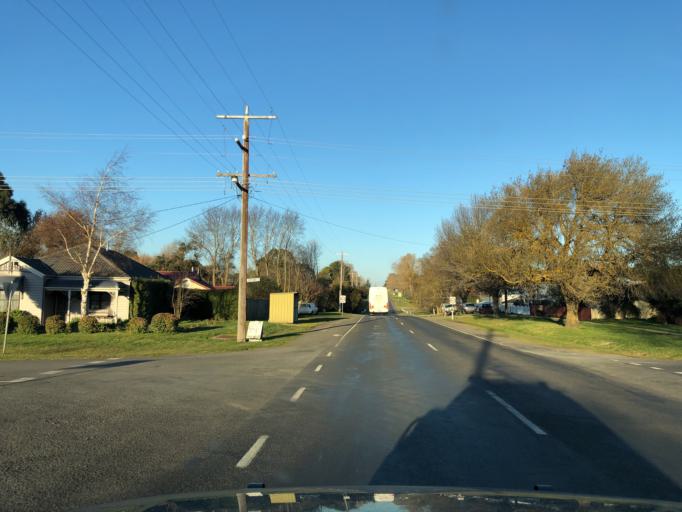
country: AU
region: Victoria
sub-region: Moorabool
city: Bacchus Marsh
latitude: -37.6002
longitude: 144.2356
